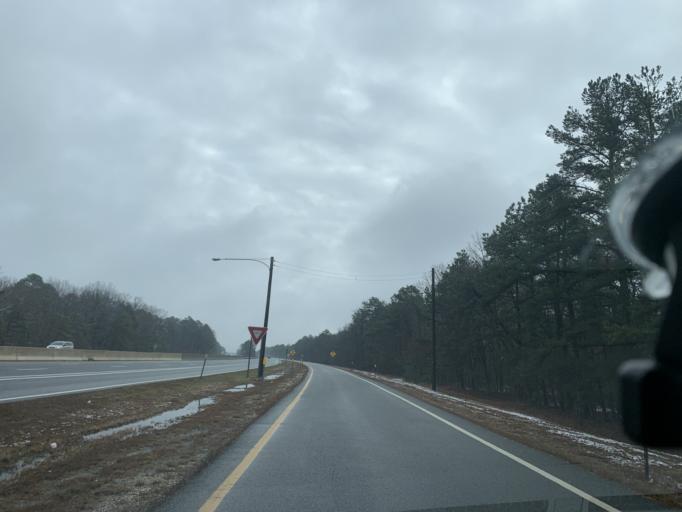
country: US
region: New Jersey
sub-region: Atlantic County
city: Pomona
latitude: 39.4460
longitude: -74.6194
